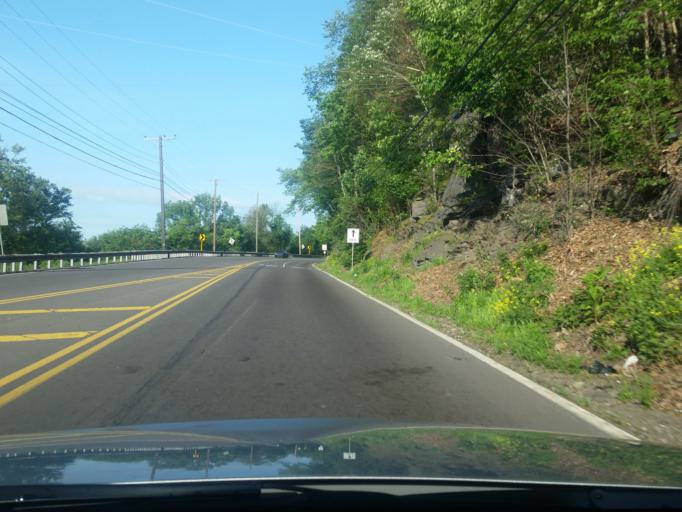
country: US
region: Pennsylvania
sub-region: Luzerne County
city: Nanticoke
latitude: 41.2253
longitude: -75.9770
